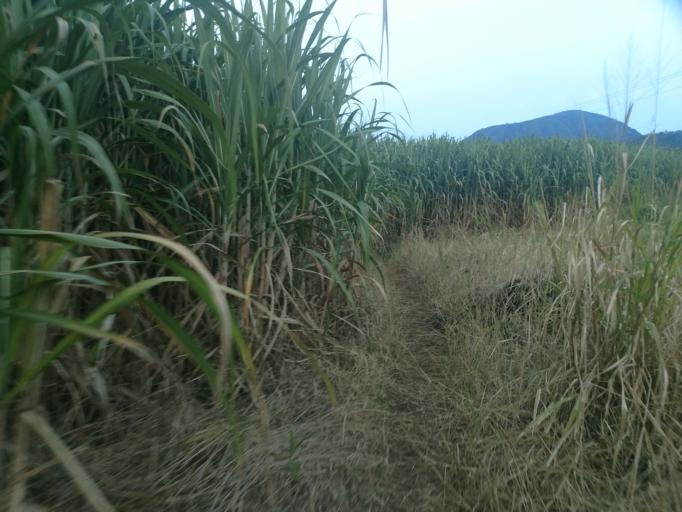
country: MX
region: Nayarit
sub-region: Tepic
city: La Corregidora
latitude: 21.4651
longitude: -104.8042
